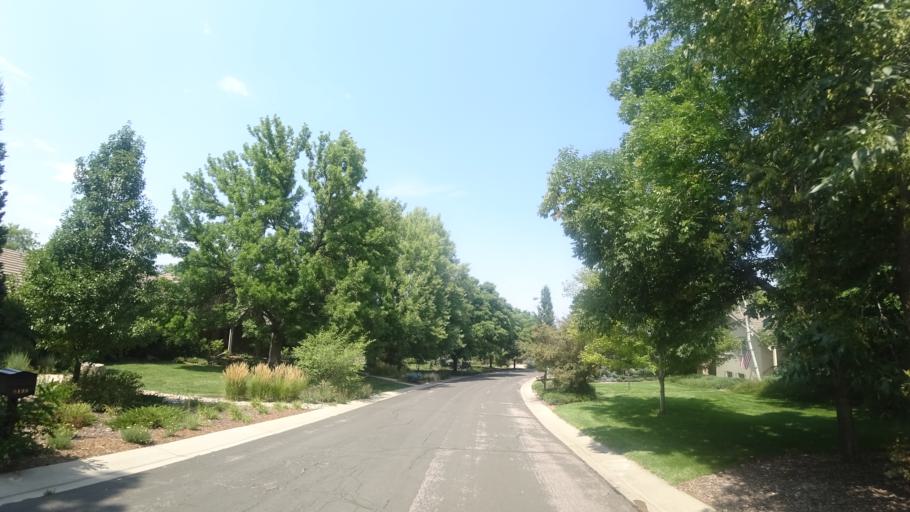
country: US
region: Colorado
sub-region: Arapahoe County
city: Greenwood Village
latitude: 39.6217
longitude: -104.9676
